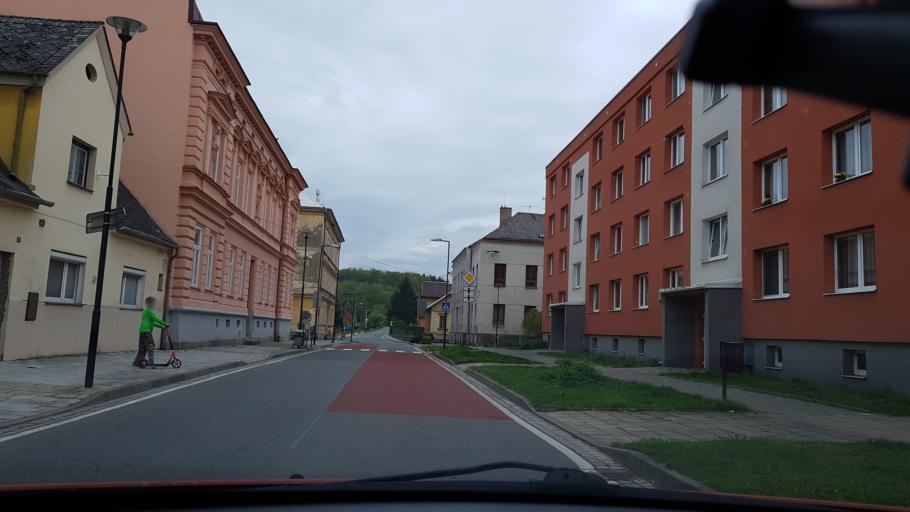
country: CZ
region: Olomoucky
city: Vidnava
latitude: 50.3721
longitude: 17.1867
